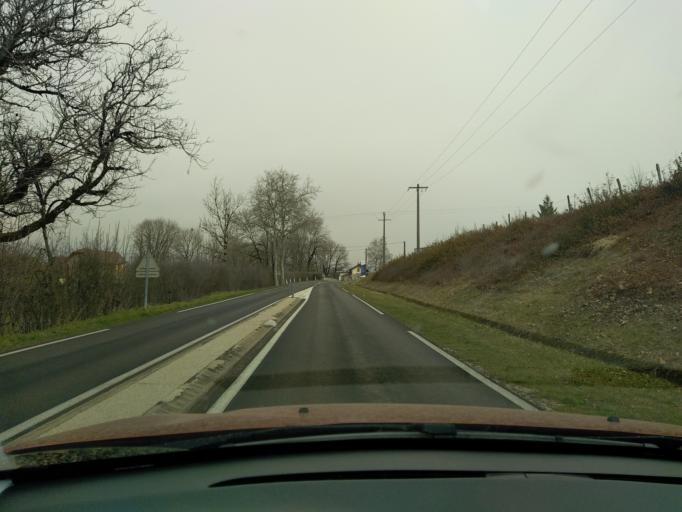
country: FR
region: Franche-Comte
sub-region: Departement du Jura
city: Champagnole
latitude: 46.7524
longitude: 5.8168
